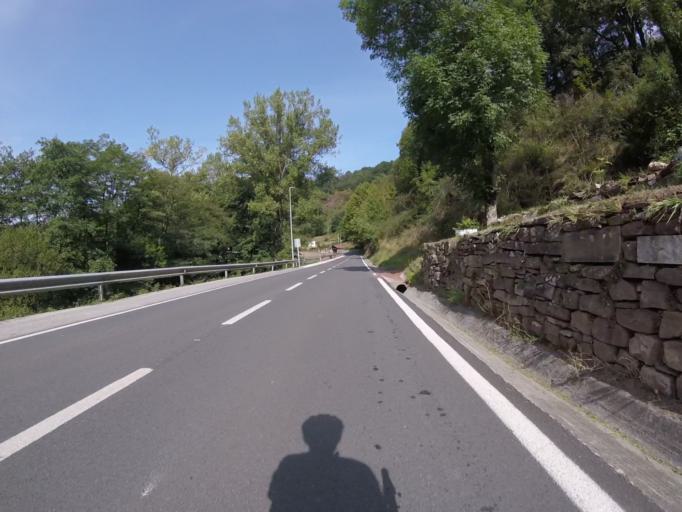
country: ES
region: Navarre
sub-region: Provincia de Navarra
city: Elgorriaga
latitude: 43.1375
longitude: -1.6820
